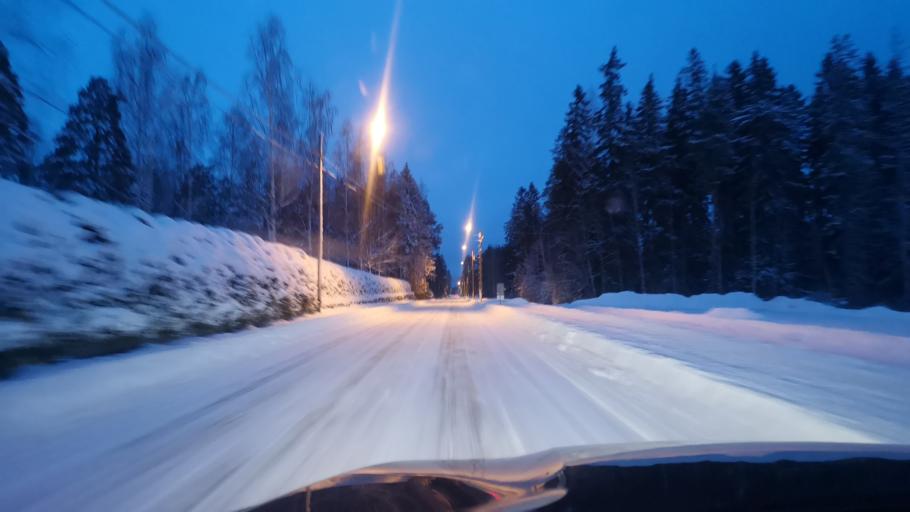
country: FI
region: Varsinais-Suomi
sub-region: Loimaa
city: Loimaa
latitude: 60.8642
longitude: 23.0823
